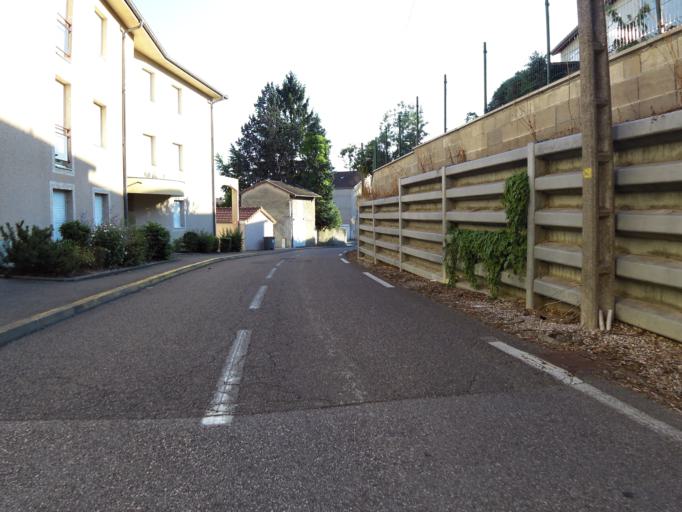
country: FR
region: Rhone-Alpes
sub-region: Departement de l'Ain
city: Meximieux
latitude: 45.9026
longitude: 5.1894
